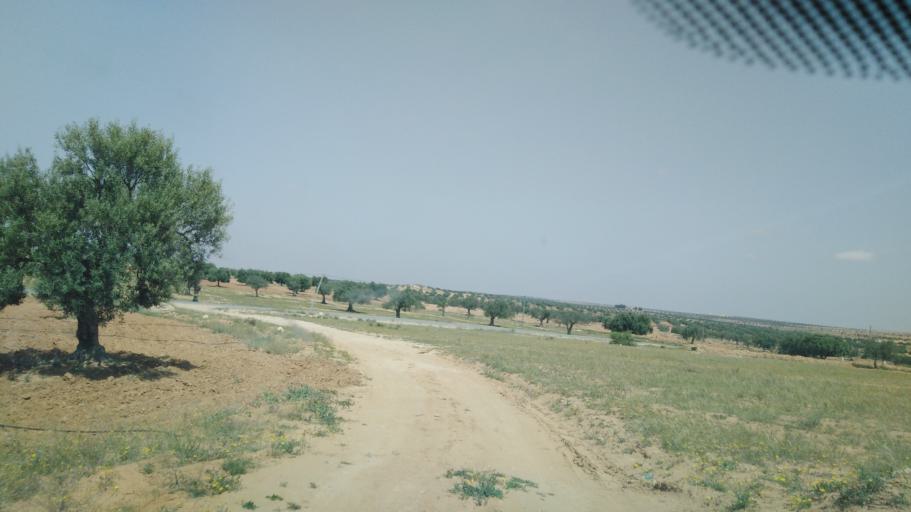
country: TN
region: Safaqis
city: Sfax
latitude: 34.7486
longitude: 10.5670
